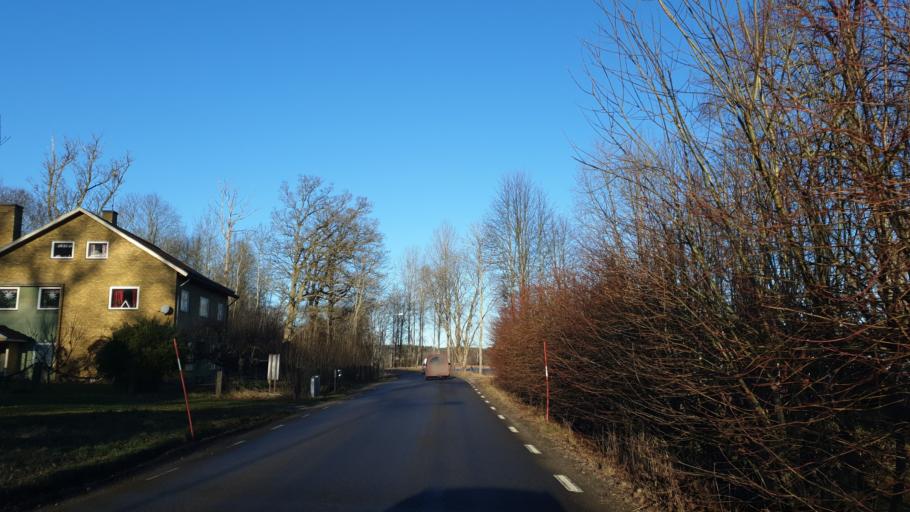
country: SE
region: Blekinge
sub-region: Karlskrona Kommun
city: Nattraby
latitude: 56.2605
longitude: 15.5111
